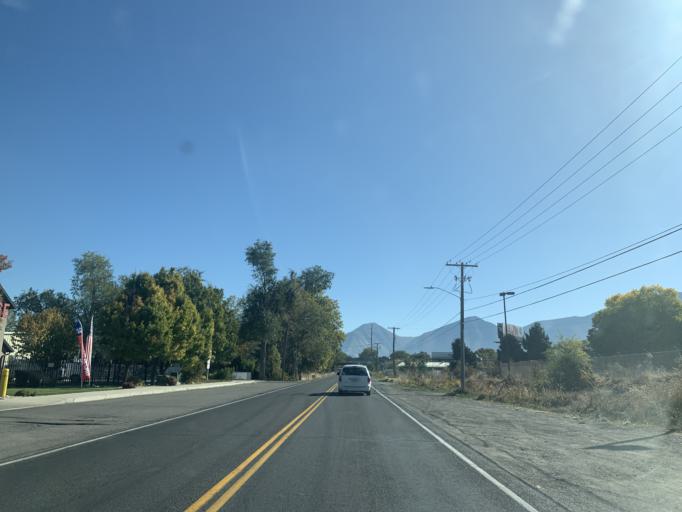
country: US
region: Utah
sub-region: Utah County
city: Payson
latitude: 40.0436
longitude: -111.7481
